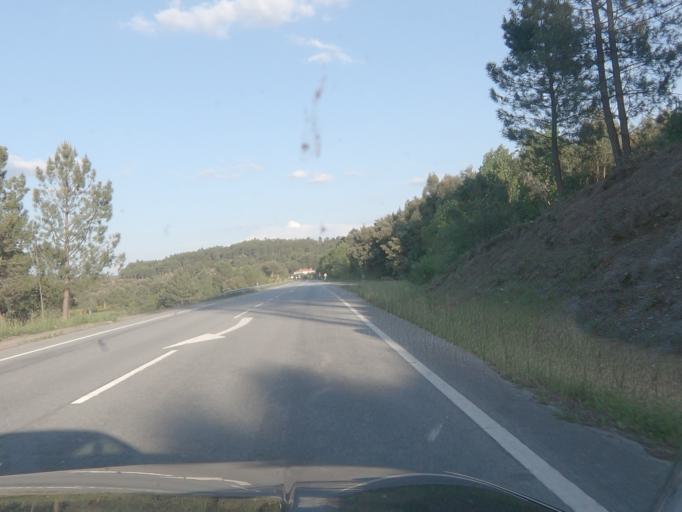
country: PT
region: Portalegre
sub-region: Marvao
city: Marvao
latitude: 39.3707
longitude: -7.3478
